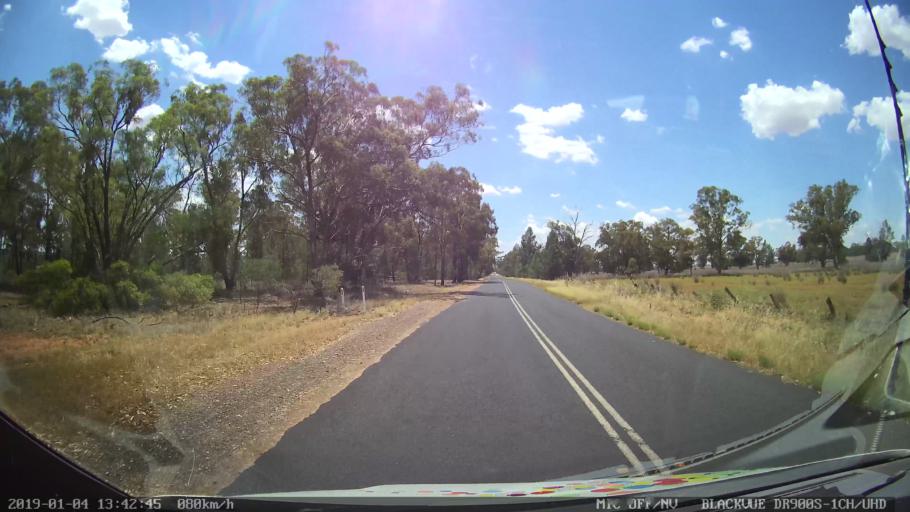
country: AU
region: New South Wales
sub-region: Dubbo Municipality
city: Dubbo
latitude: -32.4861
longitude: 148.5565
